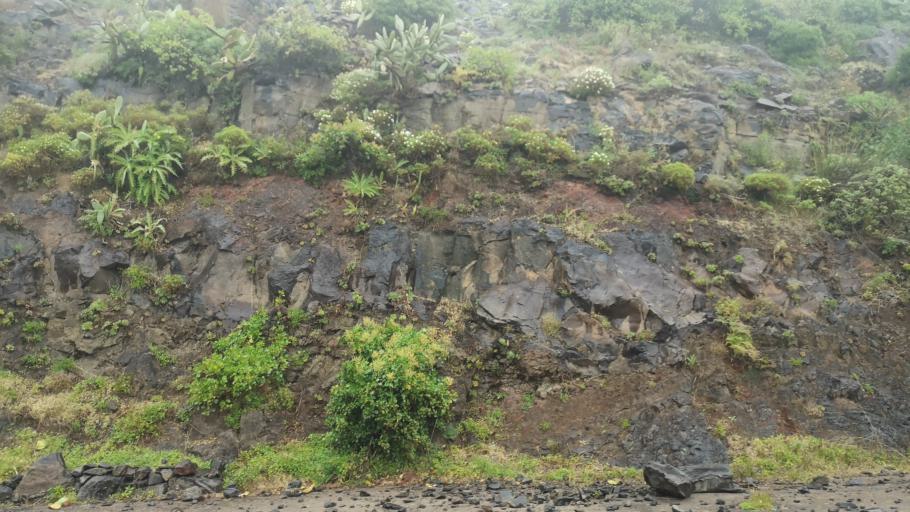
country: ES
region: Canary Islands
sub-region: Provincia de Santa Cruz de Tenerife
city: Alajero
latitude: 28.0986
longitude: -17.1893
